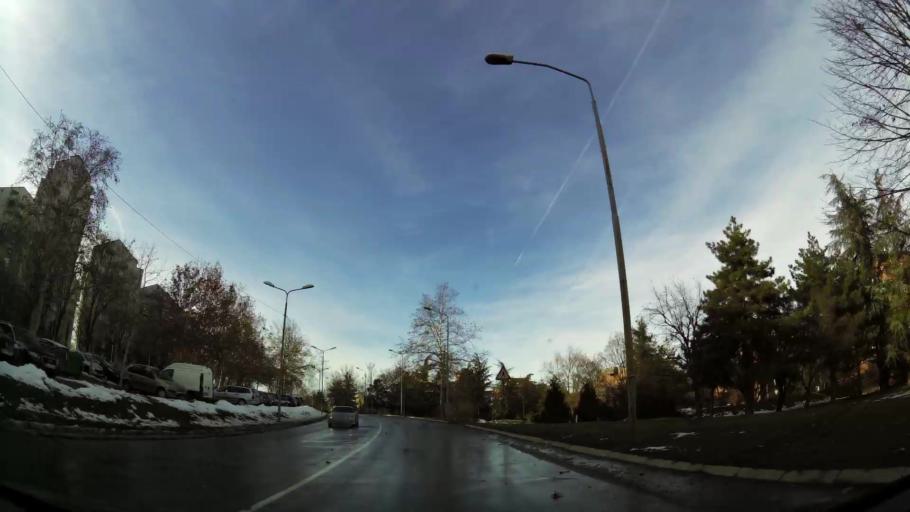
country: RS
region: Central Serbia
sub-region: Belgrade
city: Rakovica
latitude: 44.7297
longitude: 20.4245
